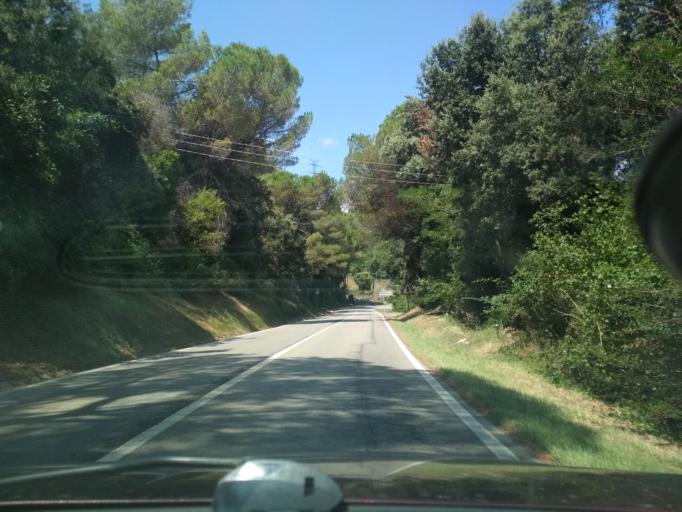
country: ES
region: Catalonia
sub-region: Provincia de Barcelona
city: Sant Feliu de Codines
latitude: 41.7062
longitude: 2.1571
